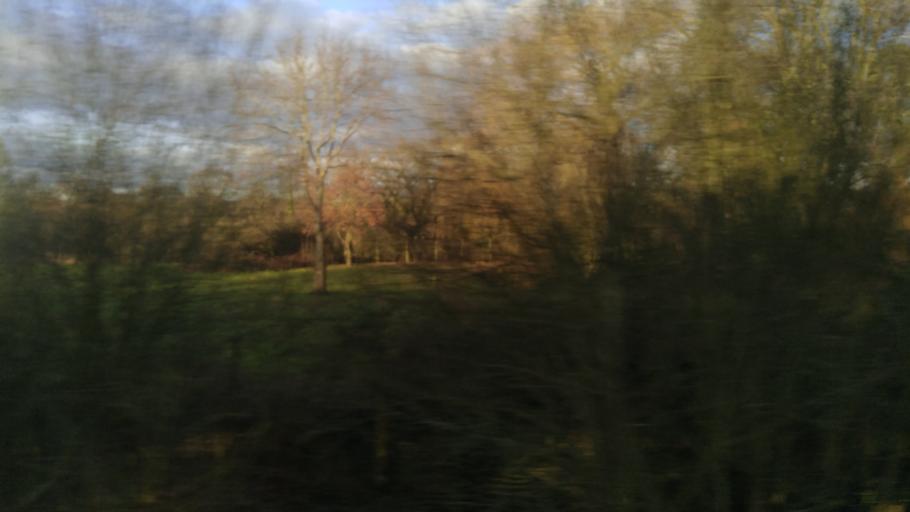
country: GB
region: England
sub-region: Kent
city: Headcorn
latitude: 51.1637
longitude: 0.6539
